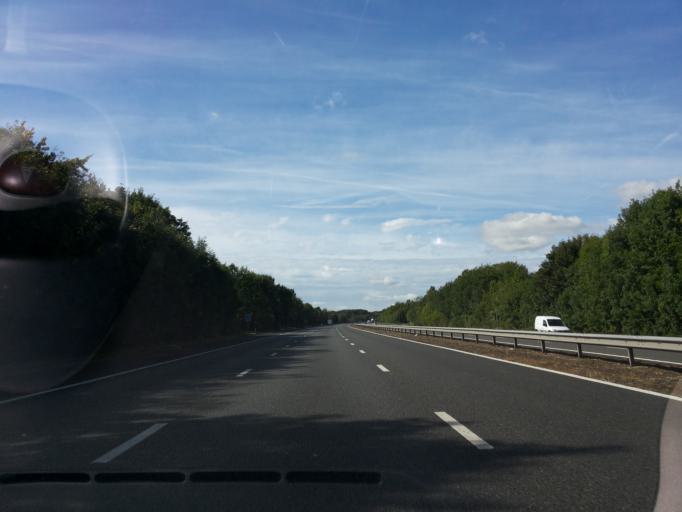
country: GB
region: England
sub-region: Kent
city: Borough Green
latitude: 51.3074
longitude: 0.3346
